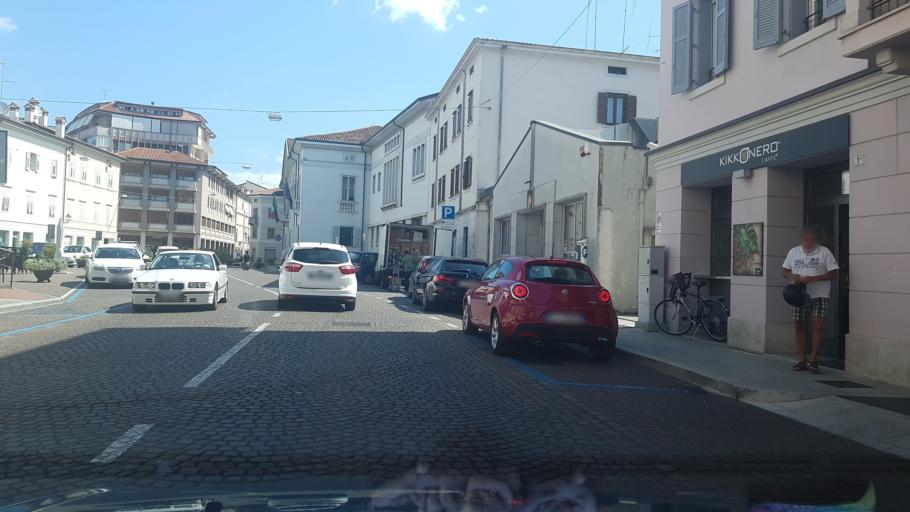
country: IT
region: Friuli Venezia Giulia
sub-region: Provincia di Gorizia
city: Gorizia
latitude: 45.9408
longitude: 13.6213
